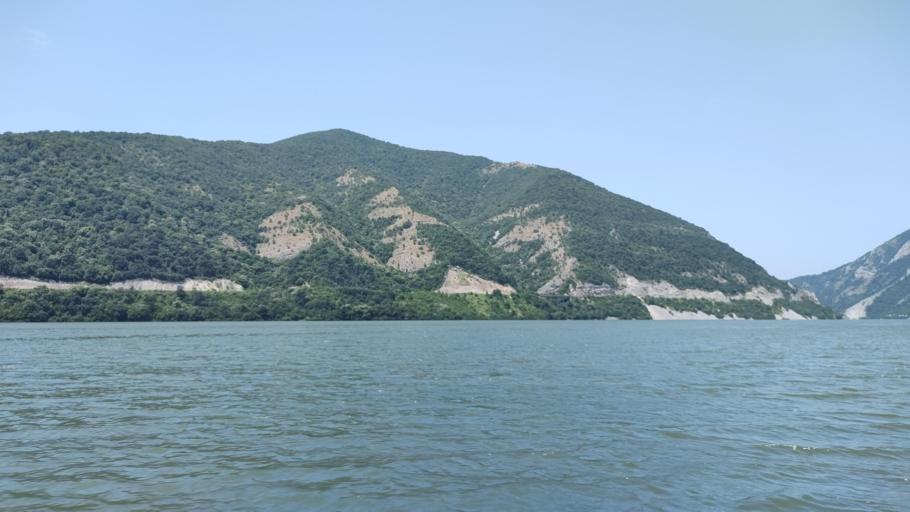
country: RO
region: Caras-Severin
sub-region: Comuna Berzasca
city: Berzasca
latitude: 44.5746
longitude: 22.0292
